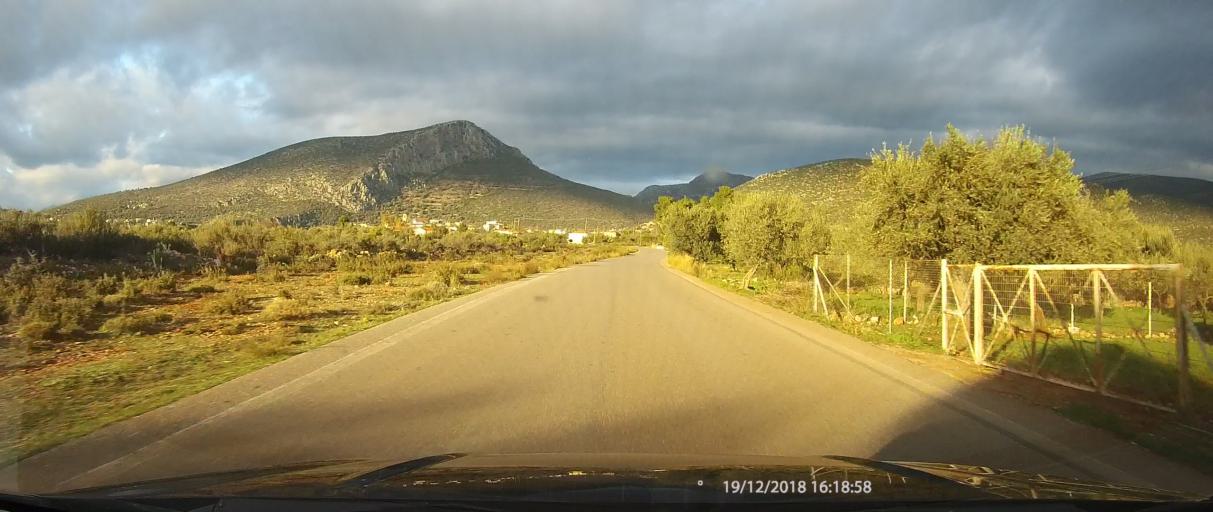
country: GR
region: Peloponnese
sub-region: Nomos Lakonias
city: Kato Glikovrisi
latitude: 36.9285
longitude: 22.8221
